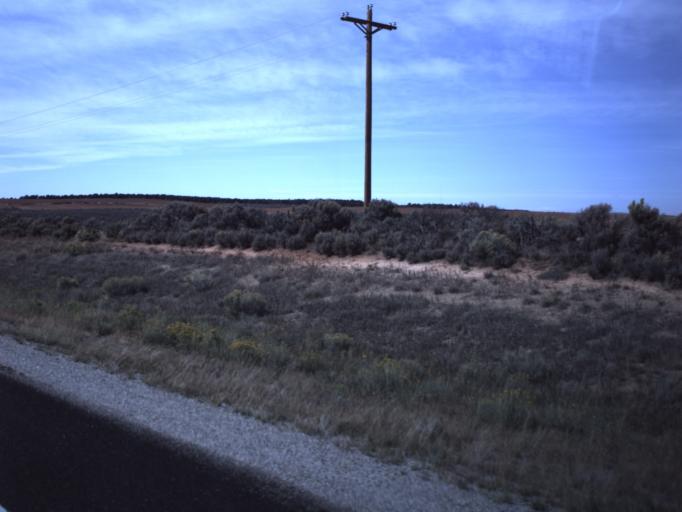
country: US
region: Utah
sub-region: San Juan County
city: Monticello
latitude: 37.8437
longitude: -109.1368
